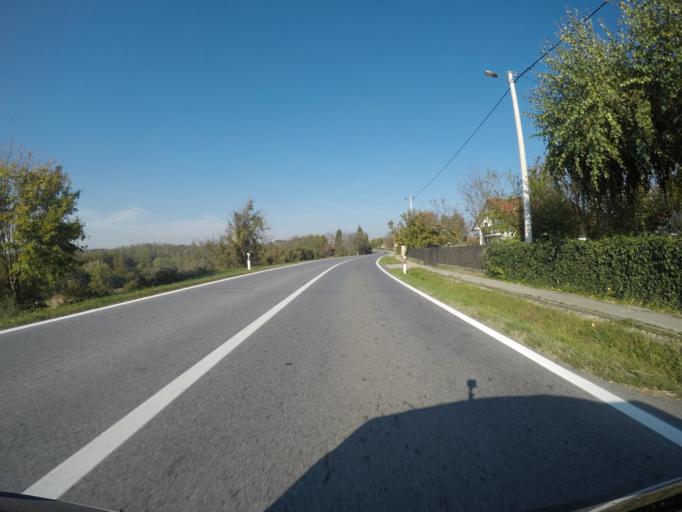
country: HR
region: Bjelovarsko-Bilogorska
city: Bjelovar
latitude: 45.9534
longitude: 16.8910
